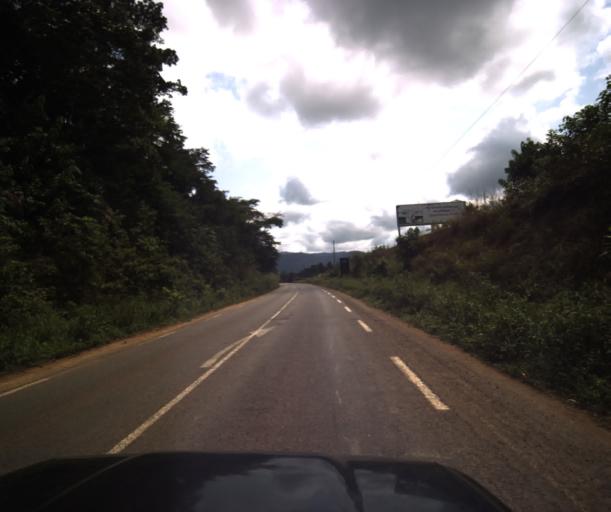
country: CM
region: Centre
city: Eseka
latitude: 3.8862
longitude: 10.7074
